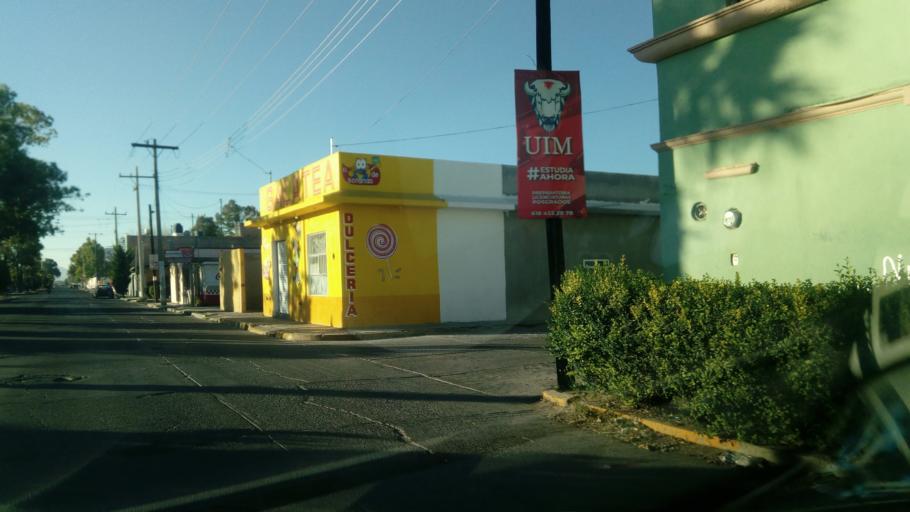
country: MX
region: Durango
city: Victoria de Durango
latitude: 24.0648
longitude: -104.5986
